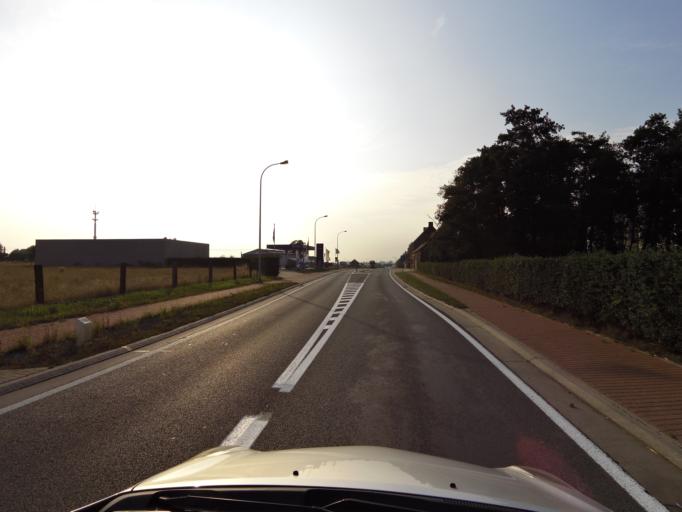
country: BE
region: Flanders
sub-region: Provincie West-Vlaanderen
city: Ardooie
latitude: 51.0067
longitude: 3.1784
